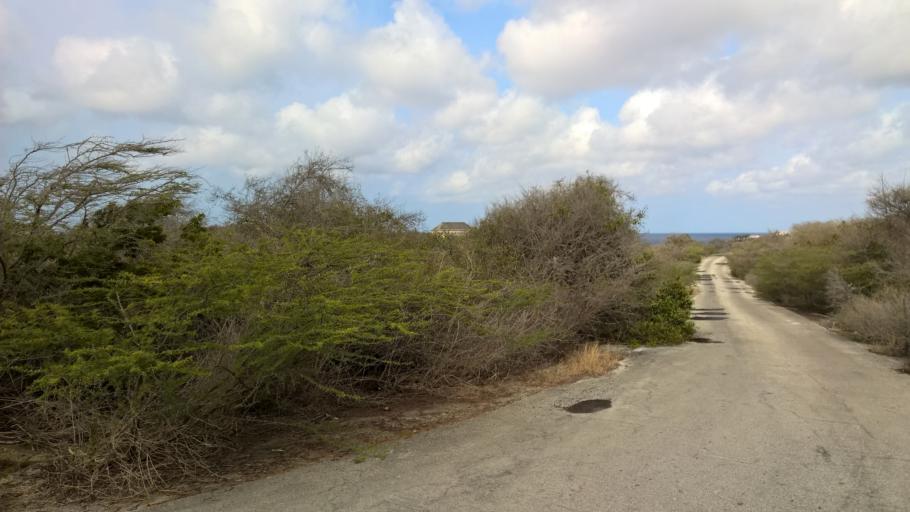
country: CW
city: Newport
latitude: 12.0697
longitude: -68.8568
